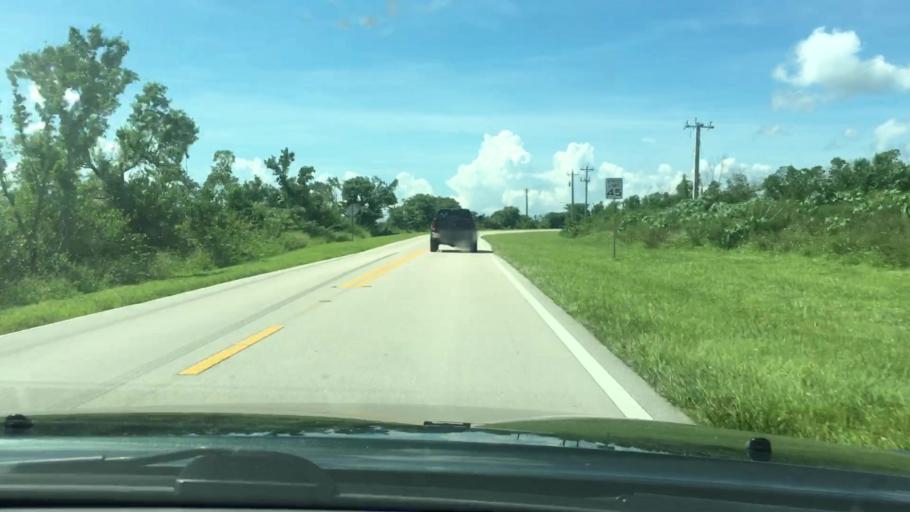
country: US
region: Florida
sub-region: Collier County
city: Marco
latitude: 25.9365
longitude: -81.6478
